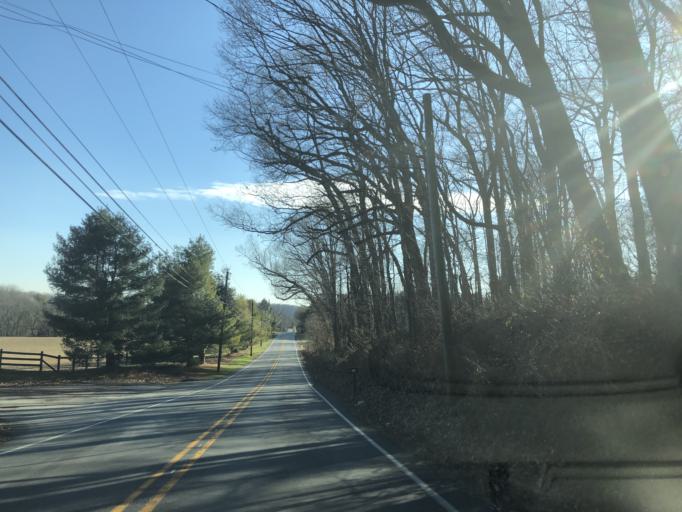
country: US
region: Pennsylvania
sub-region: Chester County
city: South Coatesville
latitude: 39.9435
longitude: -75.8344
